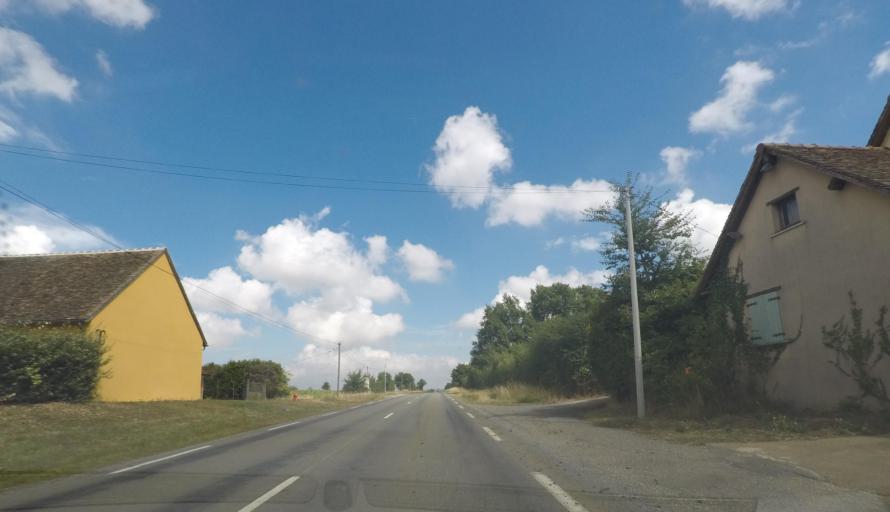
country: FR
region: Pays de la Loire
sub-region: Departement de la Sarthe
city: Saint-Cosme-en-Vairais
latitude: 48.2431
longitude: 0.4413
